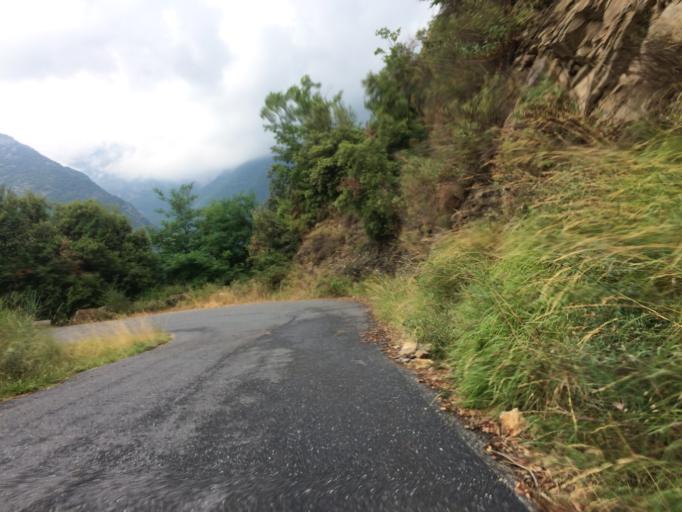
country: IT
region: Liguria
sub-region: Provincia di Imperia
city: Castel Vittorio
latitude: 43.9480
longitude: 7.6894
